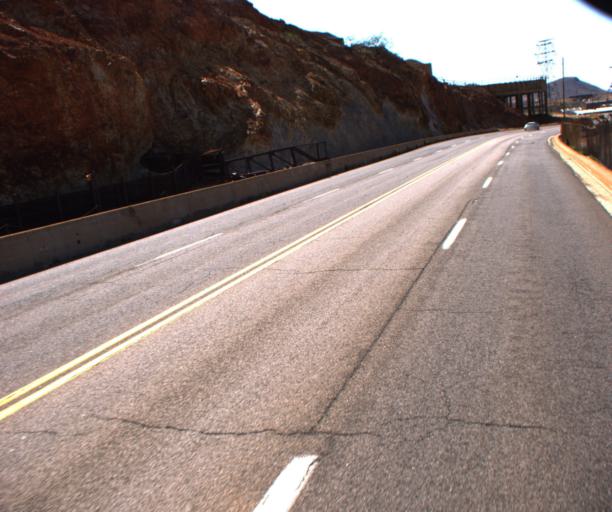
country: US
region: Arizona
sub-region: Cochise County
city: Bisbee
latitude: 31.4347
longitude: -109.8961
